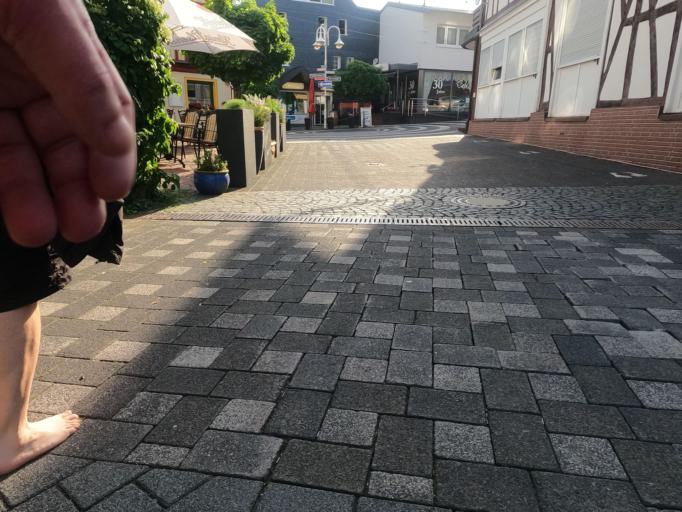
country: DE
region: Rheinland-Pfalz
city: Bad Marienberg
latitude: 50.6512
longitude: 7.9526
